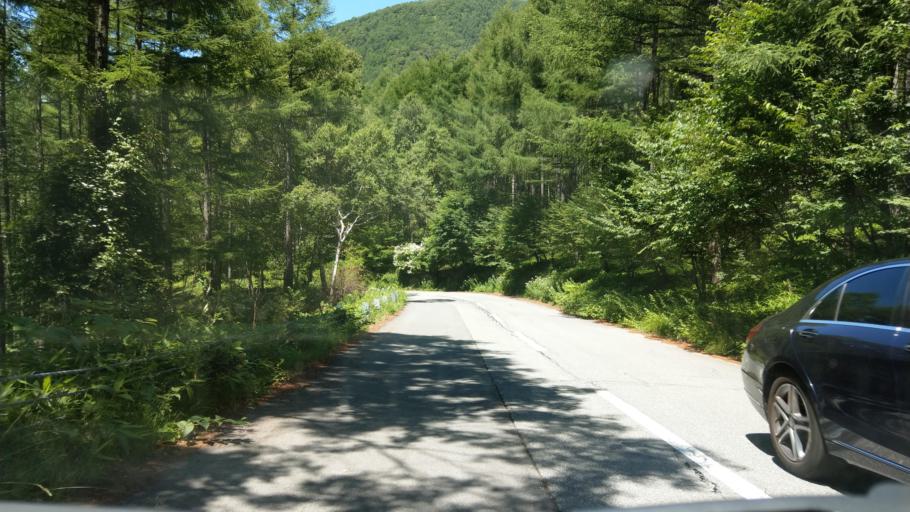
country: JP
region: Nagano
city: Komoro
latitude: 36.3956
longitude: 138.4699
